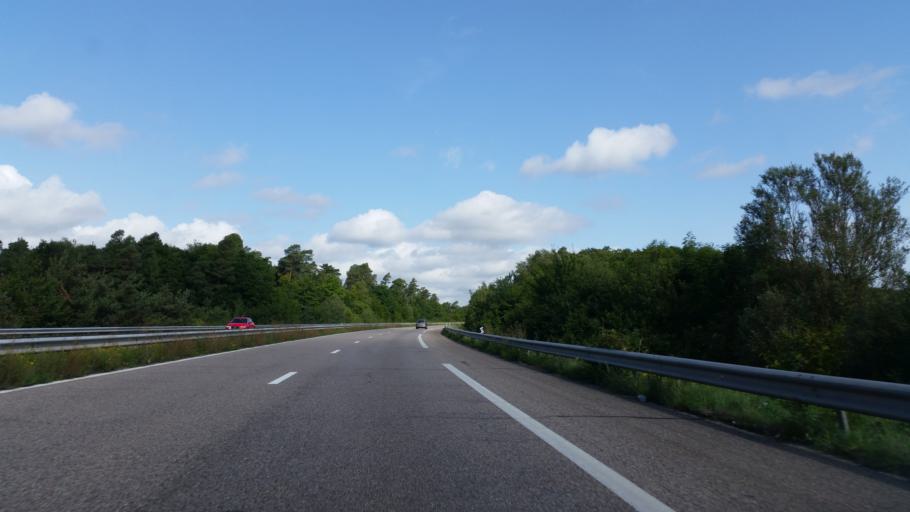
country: FR
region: Lorraine
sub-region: Departement des Vosges
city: Charmes
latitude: 48.3902
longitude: 6.2337
